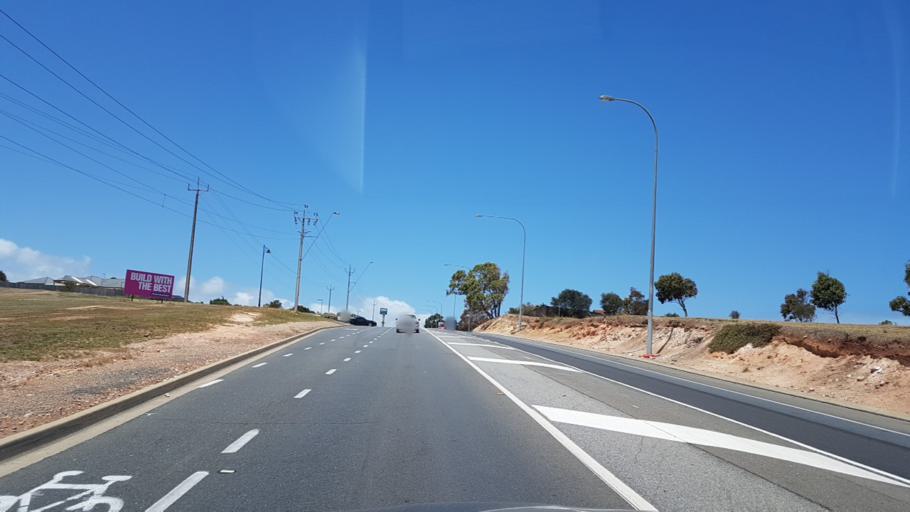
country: AU
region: South Australia
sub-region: Onkaparinga
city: Moana
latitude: -35.2113
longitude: 138.4791
